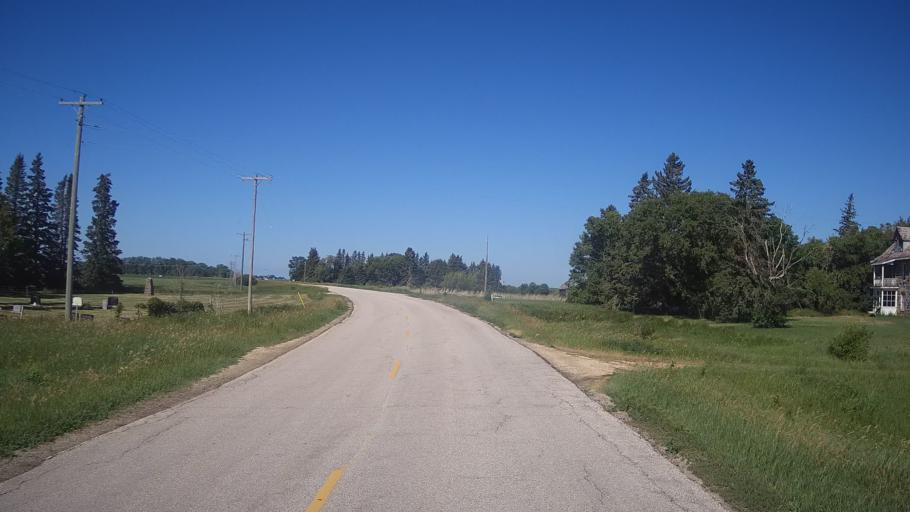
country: CA
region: Manitoba
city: Portage la Prairie
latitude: 50.0437
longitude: -98.0564
